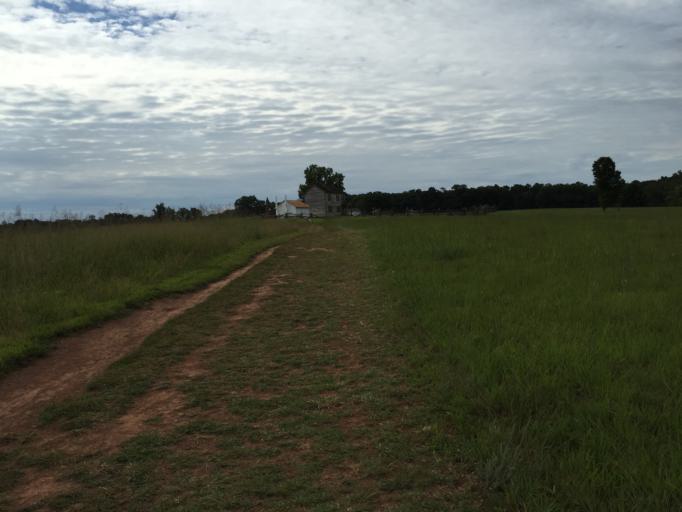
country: US
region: Virginia
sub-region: Prince William County
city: Bull Run
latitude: 38.8160
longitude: -77.5233
